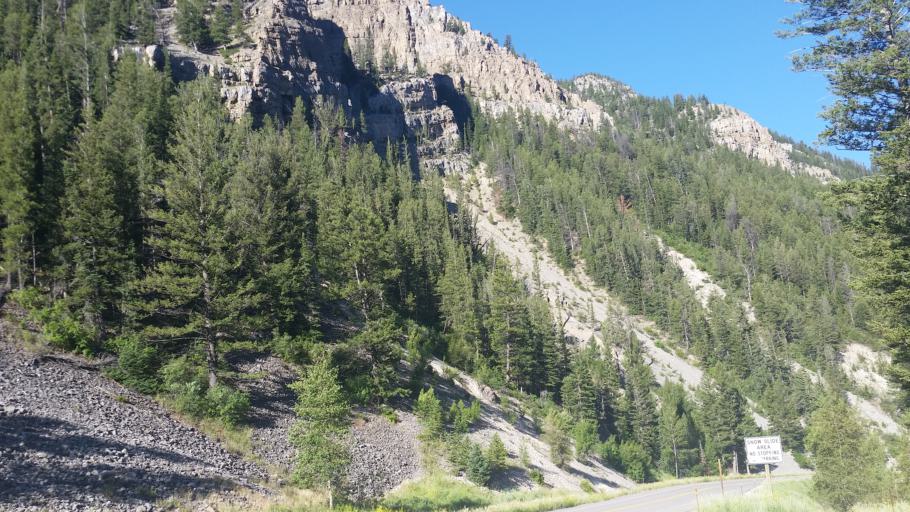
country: US
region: Wyoming
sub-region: Teton County
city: Hoback
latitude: 43.2811
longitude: -110.6145
